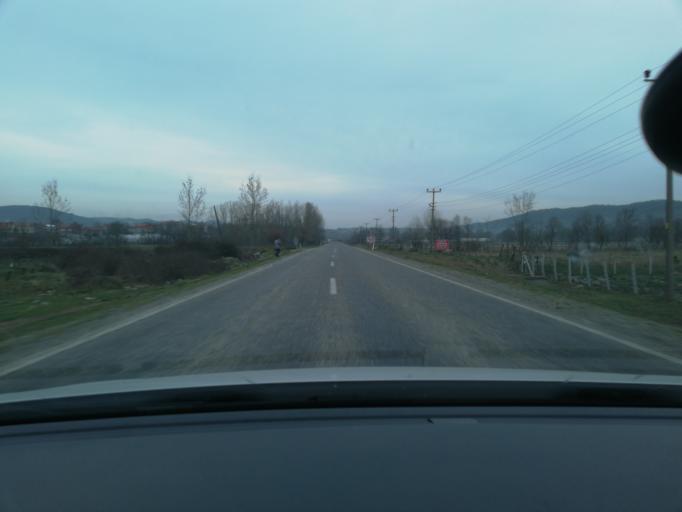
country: TR
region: Zonguldak
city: Saltukova
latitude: 41.5082
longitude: 32.1008
